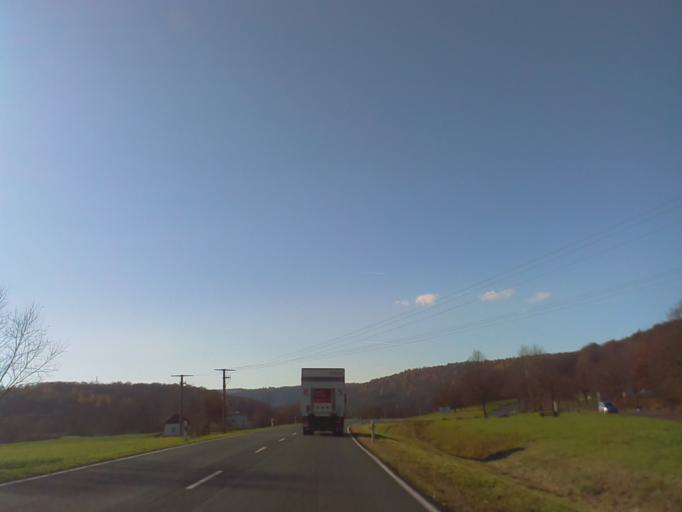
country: DE
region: Bavaria
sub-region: Regierungsbezirk Unterfranken
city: Hohenroth
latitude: 50.3045
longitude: 10.1796
